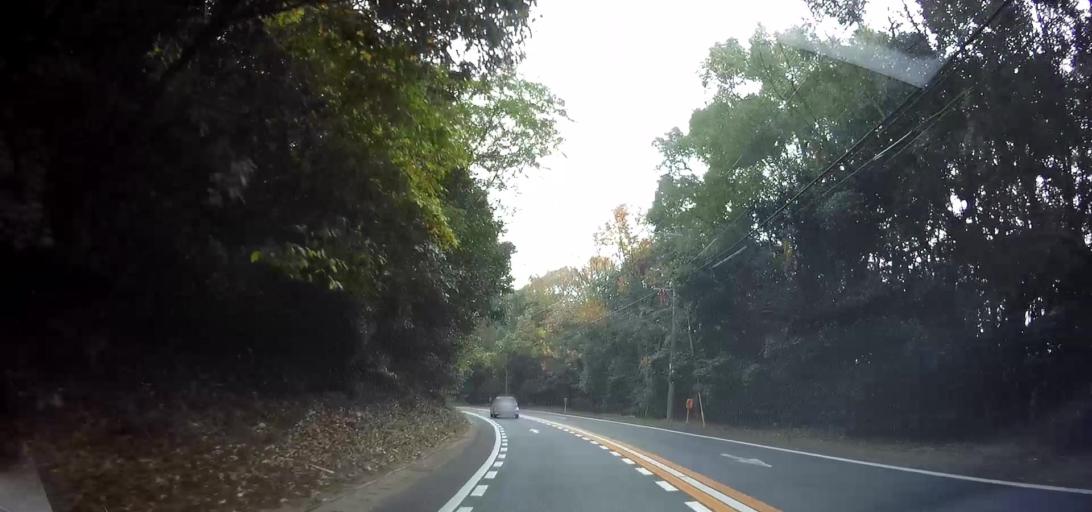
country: JP
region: Nagasaki
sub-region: Isahaya-shi
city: Isahaya
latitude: 32.7897
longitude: 130.0522
